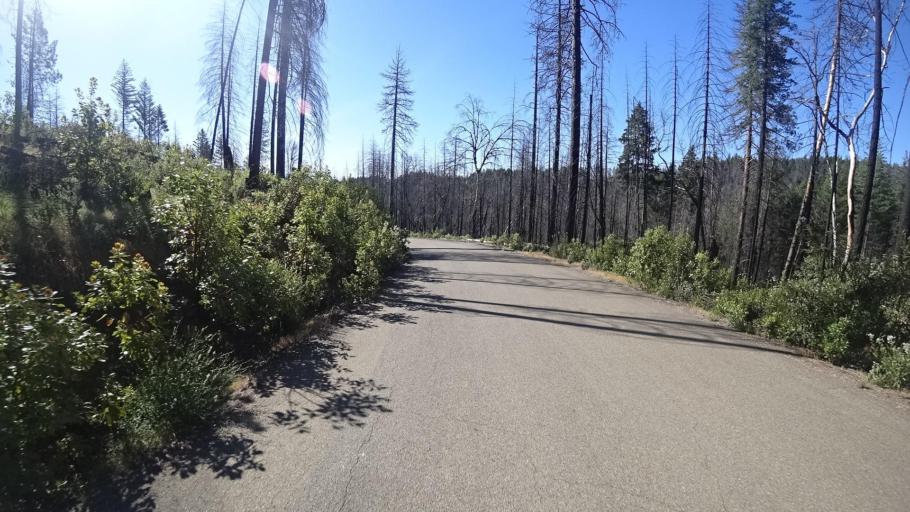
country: US
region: California
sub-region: Lake County
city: Upper Lake
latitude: 39.3974
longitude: -122.9647
